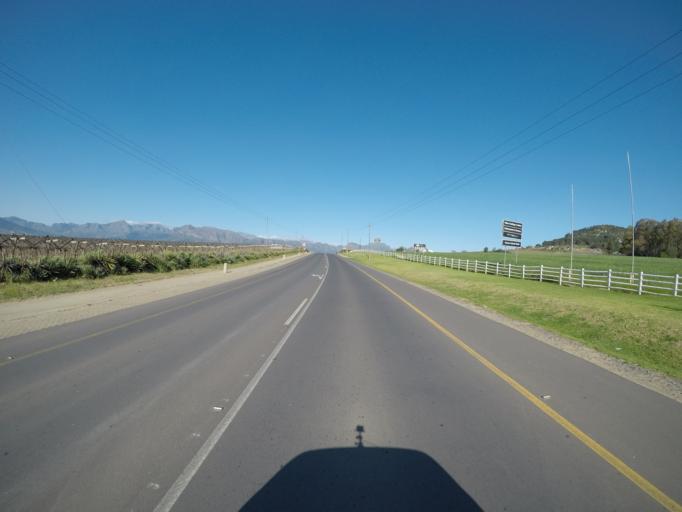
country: ZA
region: Western Cape
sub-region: Cape Winelands District Municipality
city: Noorder-Paarl
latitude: -33.6761
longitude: 18.9354
